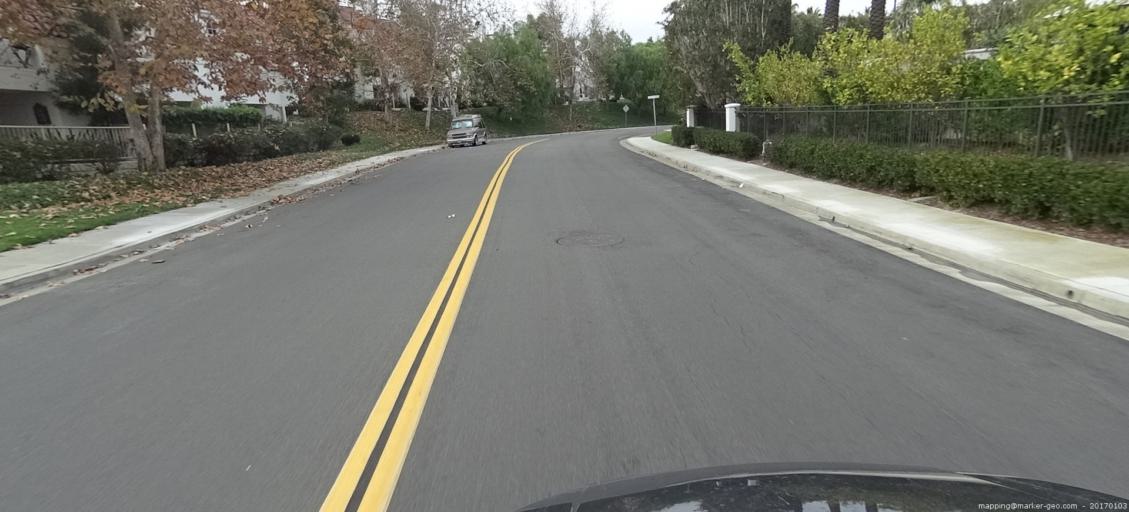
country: US
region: California
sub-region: Orange County
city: Dana Point
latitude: 33.4882
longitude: -117.6930
